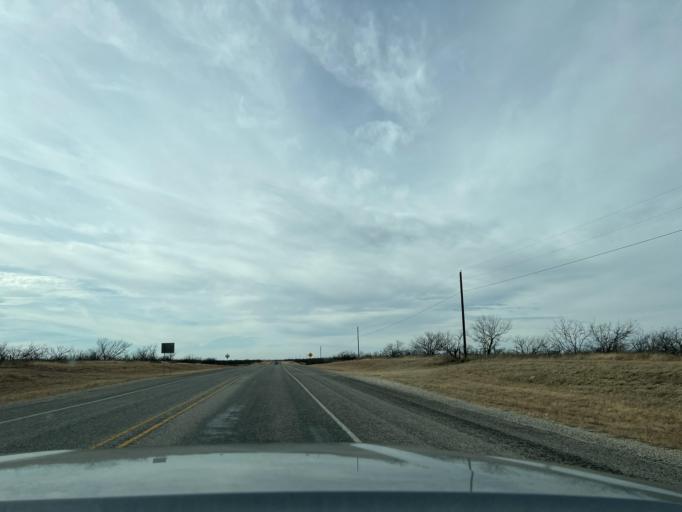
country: US
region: Texas
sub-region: Shackelford County
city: Albany
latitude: 32.7084
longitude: -99.4318
